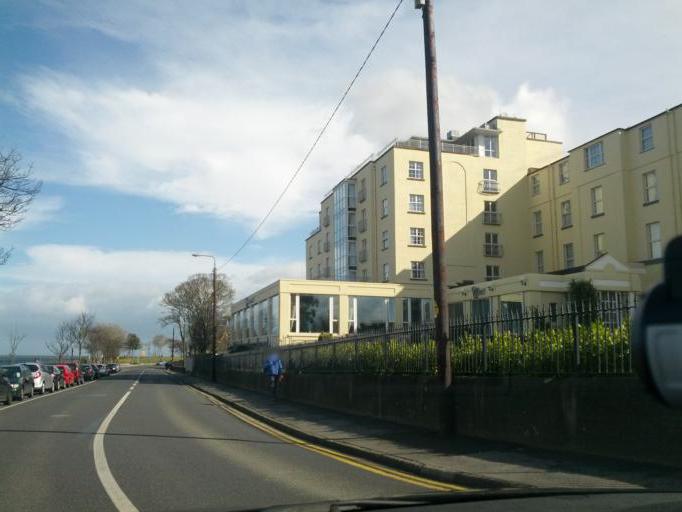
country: IE
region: Leinster
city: Malahide
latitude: 53.4512
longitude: -6.1483
